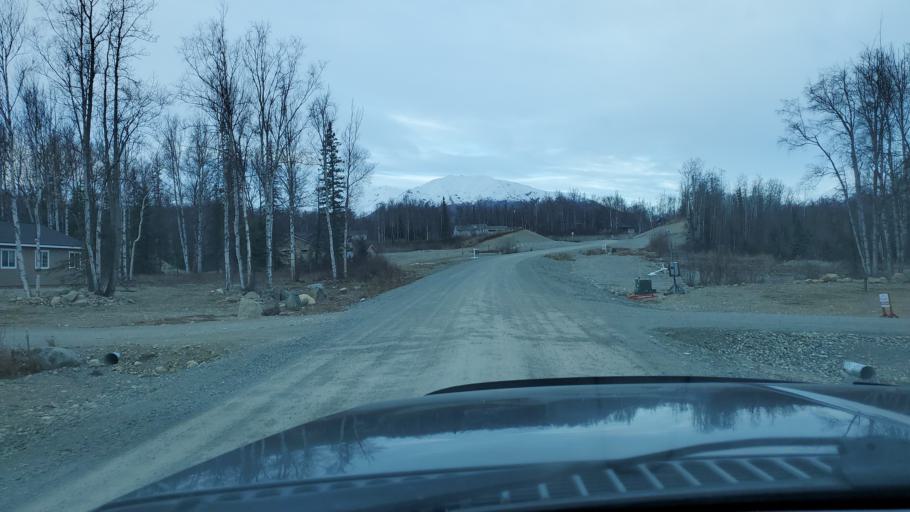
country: US
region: Alaska
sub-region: Matanuska-Susitna Borough
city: Lakes
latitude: 61.6548
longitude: -149.2910
